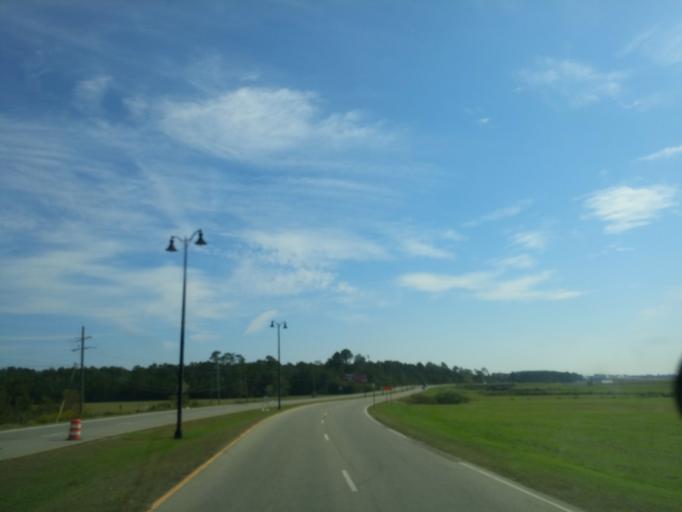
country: US
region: Mississippi
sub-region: Harrison County
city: West Gulfport
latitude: 30.4200
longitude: -89.0878
